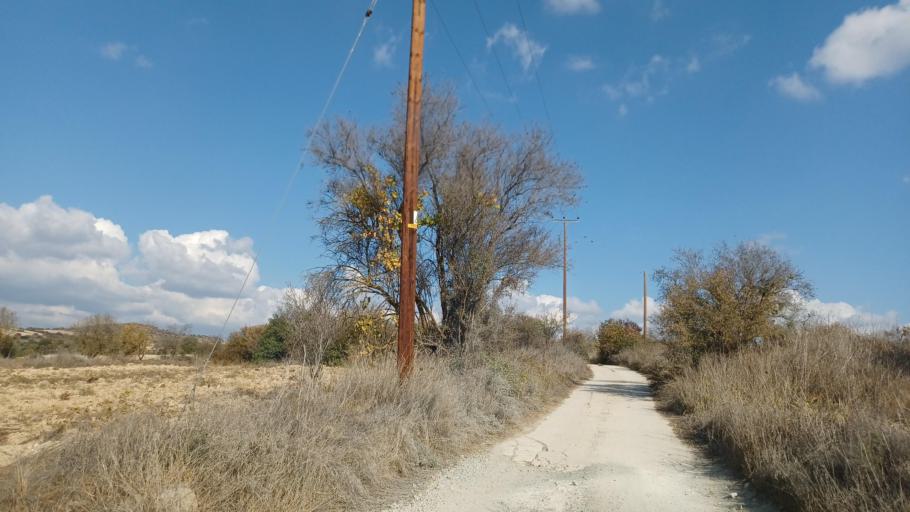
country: CY
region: Pafos
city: Mesogi
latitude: 34.8365
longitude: 32.5659
